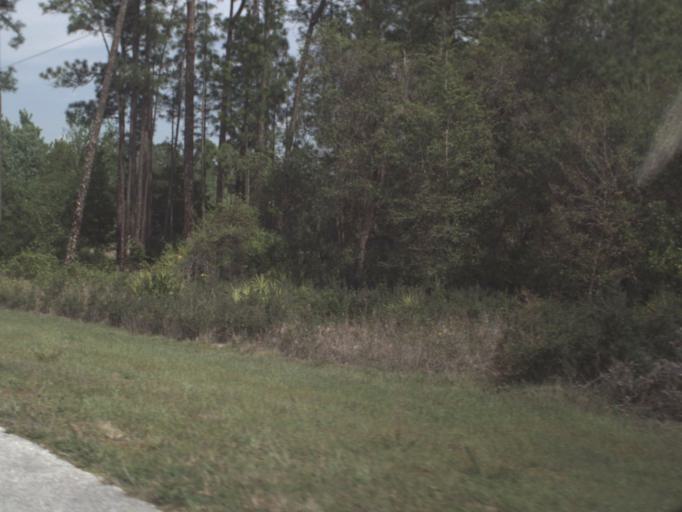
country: US
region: Florida
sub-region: Putnam County
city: Crescent City
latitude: 29.3298
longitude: -81.7103
